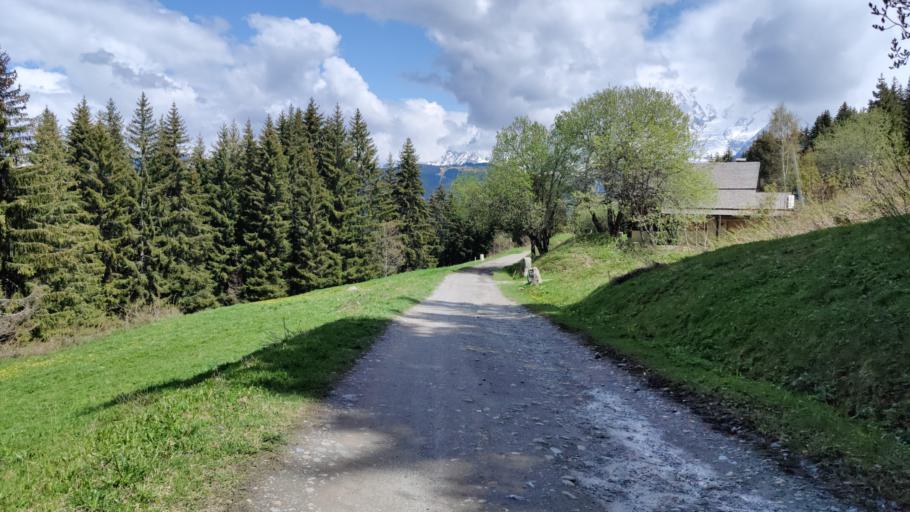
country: FR
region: Rhone-Alpes
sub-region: Departement de la Haute-Savoie
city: Saint-Gervais-les-Bains
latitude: 45.8776
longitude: 6.6758
